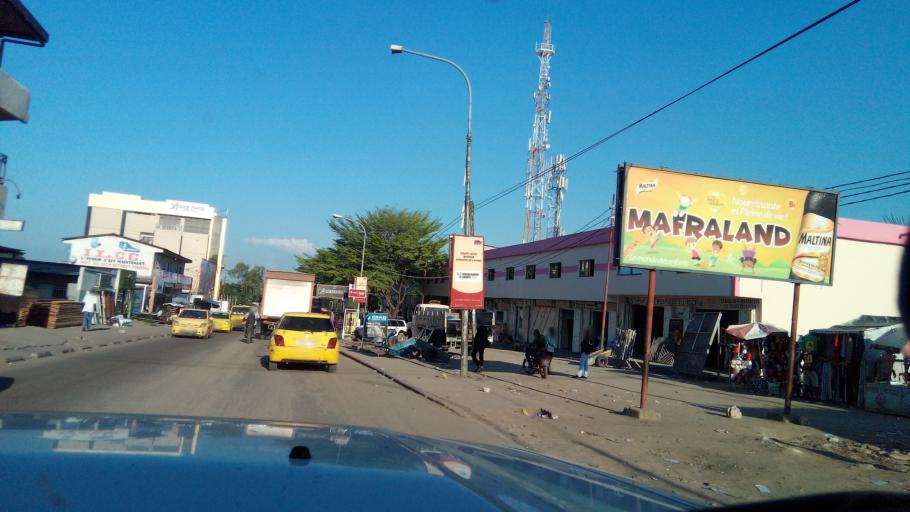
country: CD
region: Kinshasa
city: Kinshasa
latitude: -4.3462
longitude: 15.2653
